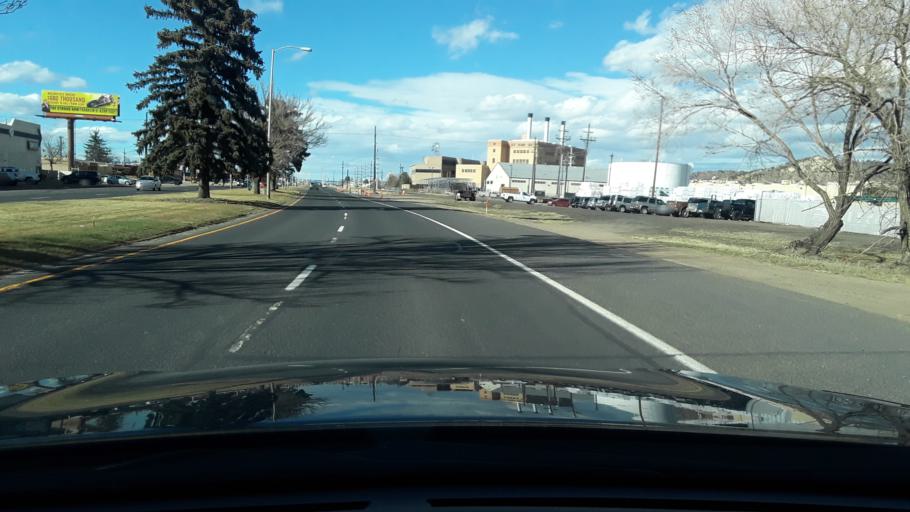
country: US
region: Colorado
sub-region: El Paso County
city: Colorado Springs
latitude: 38.8778
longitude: -104.8185
